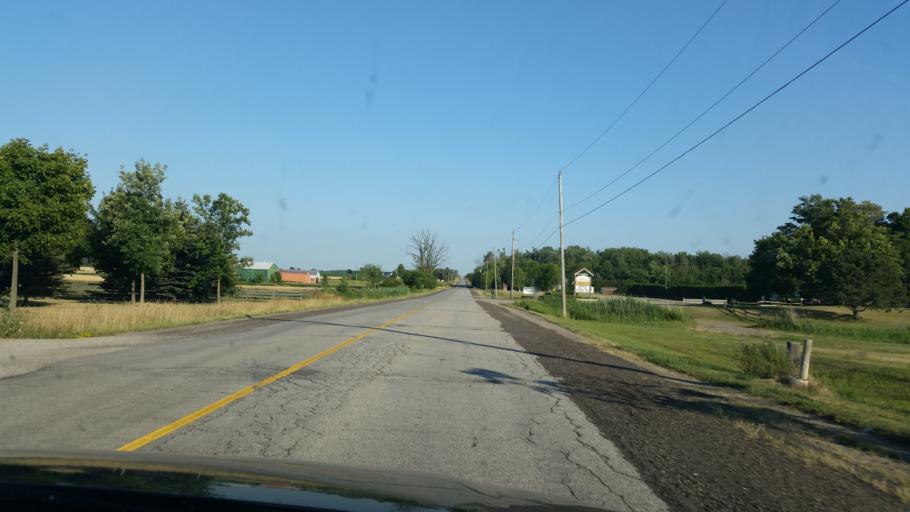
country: CA
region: Ontario
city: Brampton
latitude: 43.7869
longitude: -79.8494
